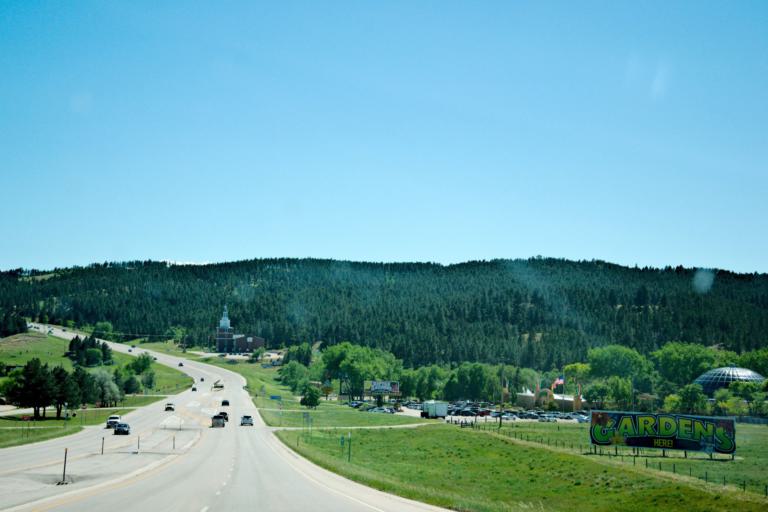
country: US
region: South Dakota
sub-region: Pennington County
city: Colonial Pine Hills
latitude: 43.9916
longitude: -103.2702
